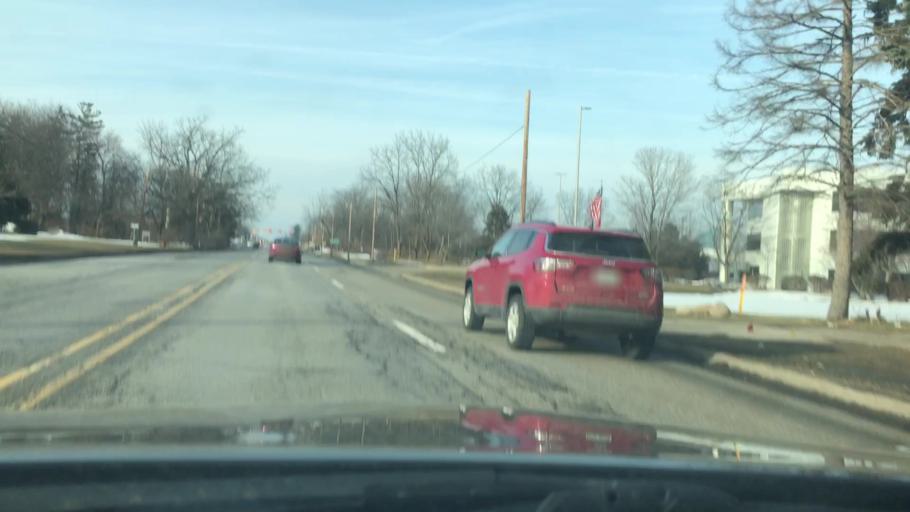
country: US
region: Michigan
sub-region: Oakland County
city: Novi
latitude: 42.4506
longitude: -83.4342
